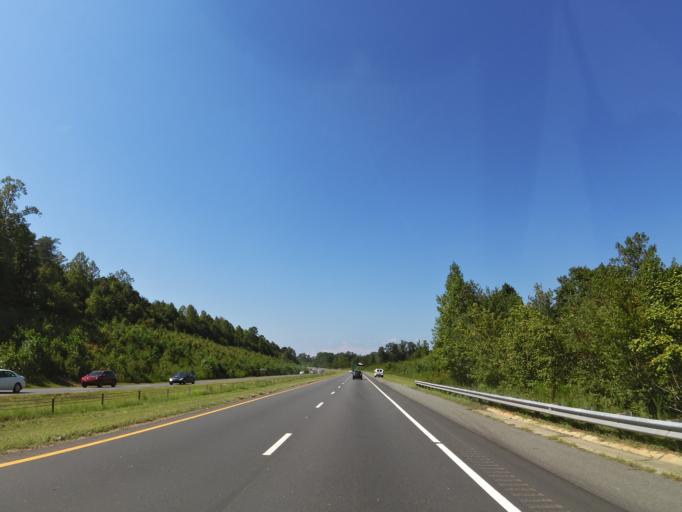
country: US
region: North Carolina
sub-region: Catawba County
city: Newton
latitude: 35.6229
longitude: -81.2893
